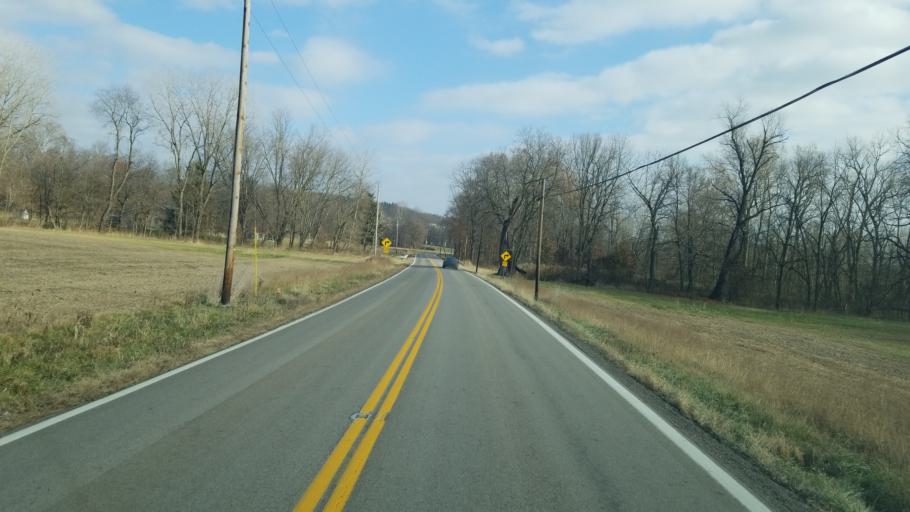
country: US
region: Ohio
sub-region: Licking County
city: Utica
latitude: 40.1607
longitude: -82.4623
